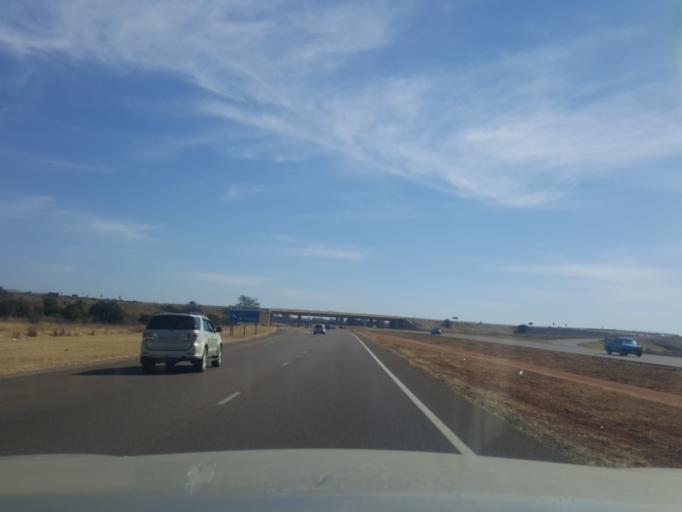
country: ZA
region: Gauteng
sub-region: City of Tshwane Metropolitan Municipality
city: Pretoria
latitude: -25.6466
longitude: 28.1568
